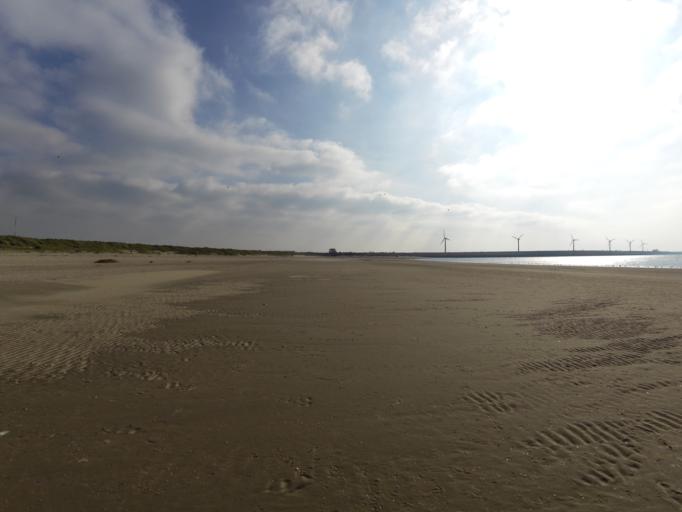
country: NL
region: South Holland
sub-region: Gemeente Hellevoetsluis
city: Nieuw-Helvoet
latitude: 51.8508
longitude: 4.0668
